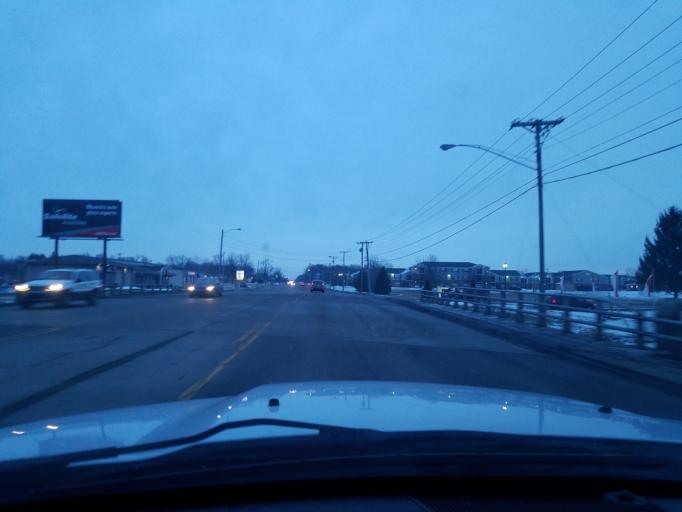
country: US
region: Indiana
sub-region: Delaware County
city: Muncie
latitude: 40.2190
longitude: -85.3692
